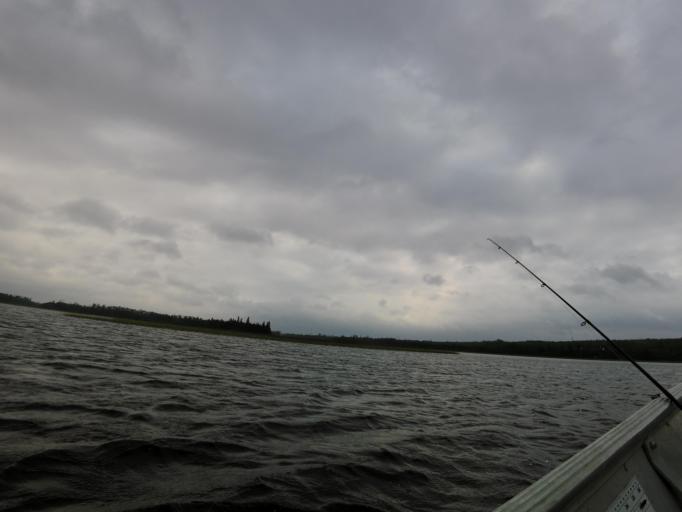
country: CA
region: Ontario
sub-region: Rainy River District
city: Atikokan
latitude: 49.5866
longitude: -91.3746
